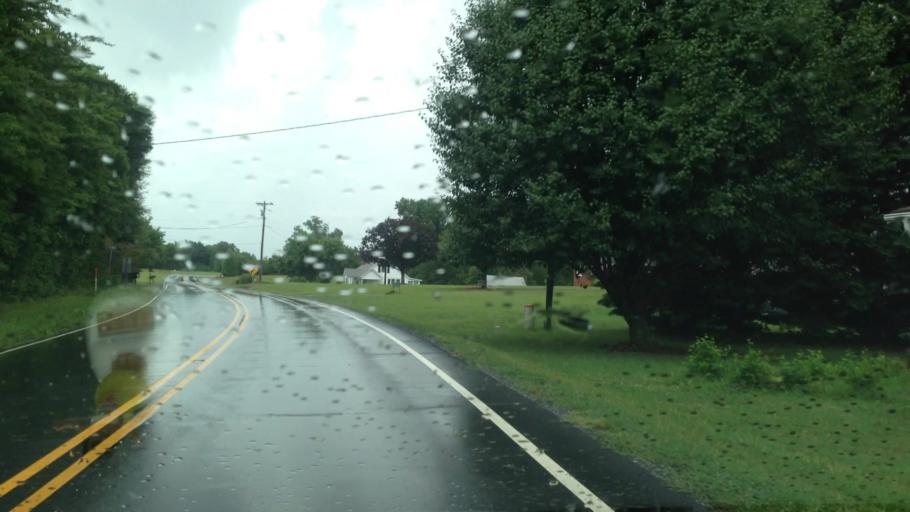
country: US
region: North Carolina
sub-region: Stokes County
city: Danbury
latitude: 36.4567
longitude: -80.0990
